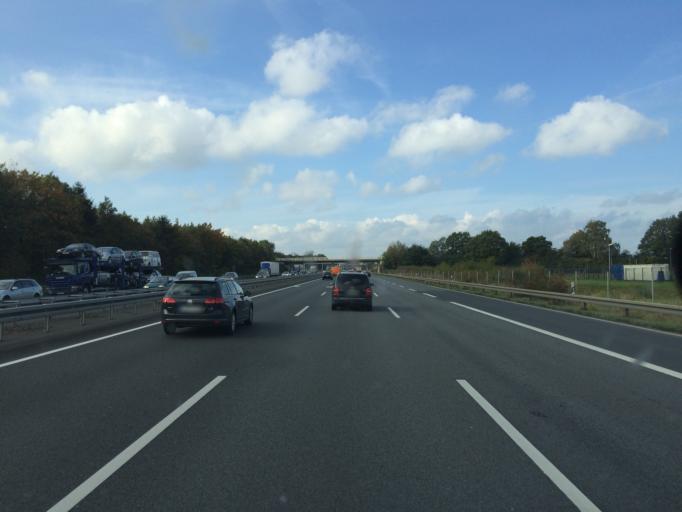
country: DE
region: Lower Saxony
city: Klein Schwulper
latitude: 52.3267
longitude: 10.4668
